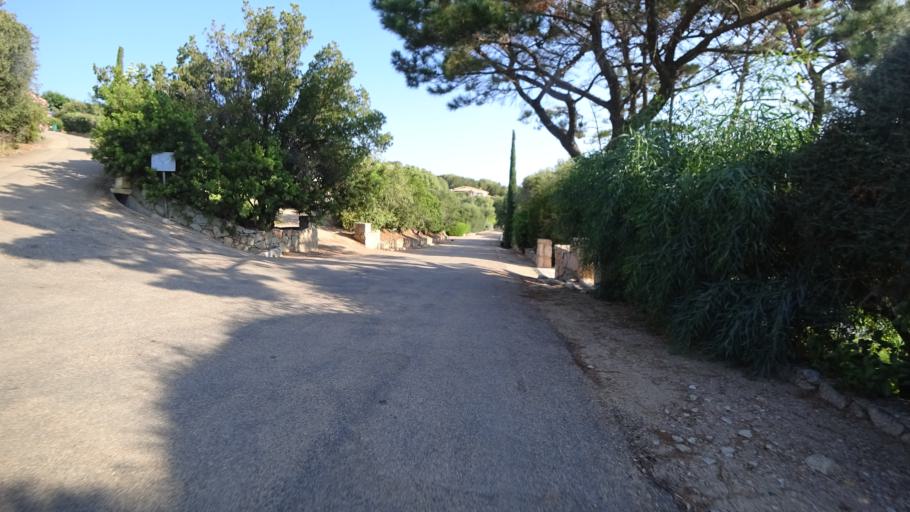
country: FR
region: Corsica
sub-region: Departement de la Corse-du-Sud
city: Porto-Vecchio
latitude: 41.6216
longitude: 9.3528
